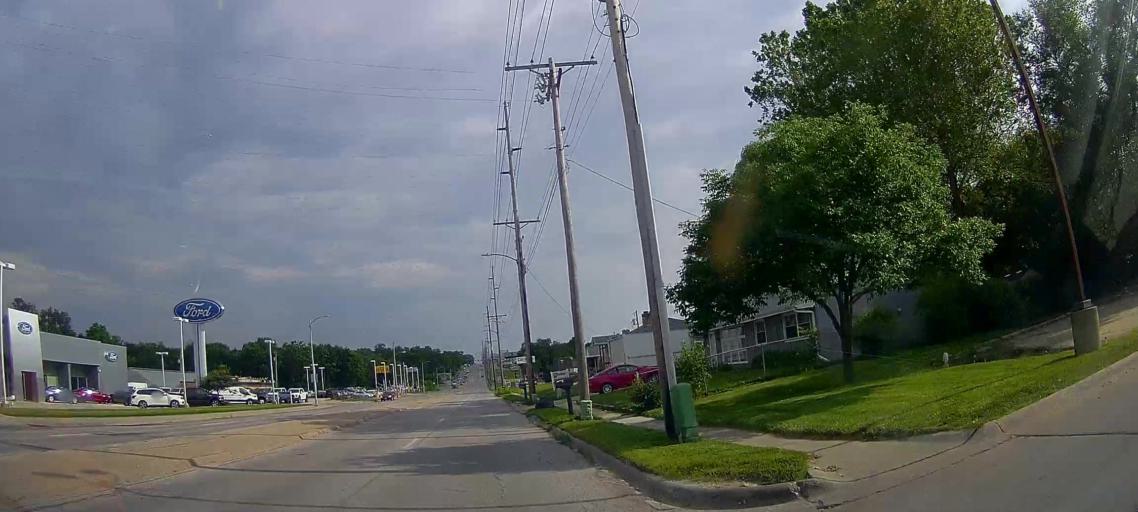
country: US
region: Nebraska
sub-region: Douglas County
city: Ralston
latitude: 41.2916
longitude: -96.0240
